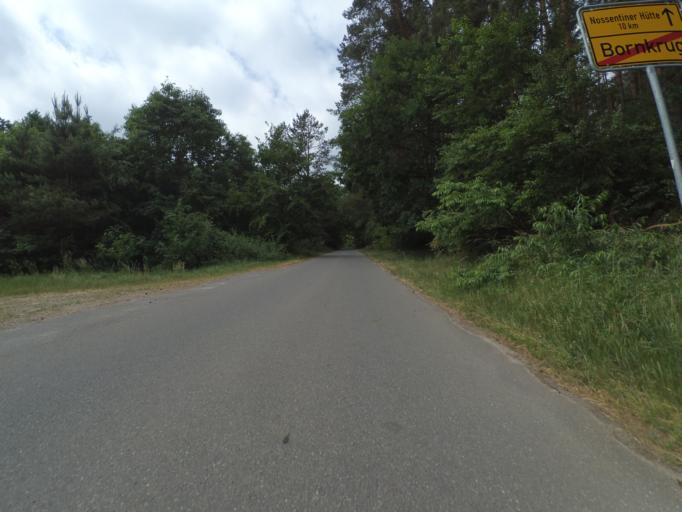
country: DE
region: Mecklenburg-Vorpommern
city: Krakow am See
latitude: 53.5971
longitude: 12.3854
